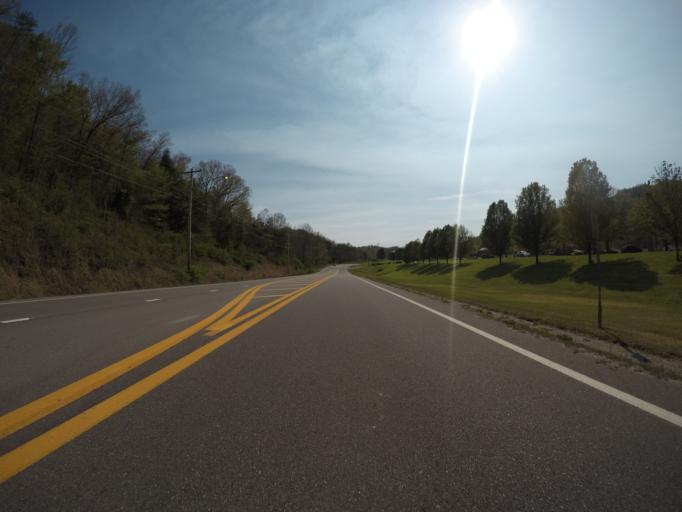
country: US
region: West Virginia
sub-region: Kanawha County
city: Charleston
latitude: 38.3734
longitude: -81.5733
